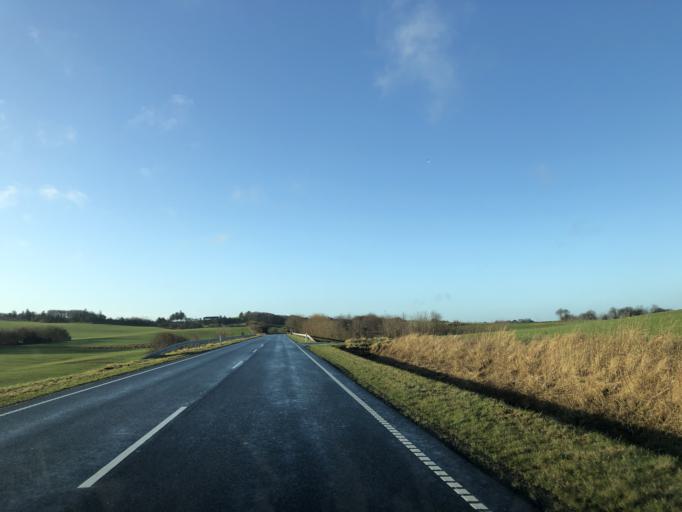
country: DK
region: Central Jutland
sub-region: Lemvig Kommune
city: Lemvig
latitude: 56.5589
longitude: 8.4494
